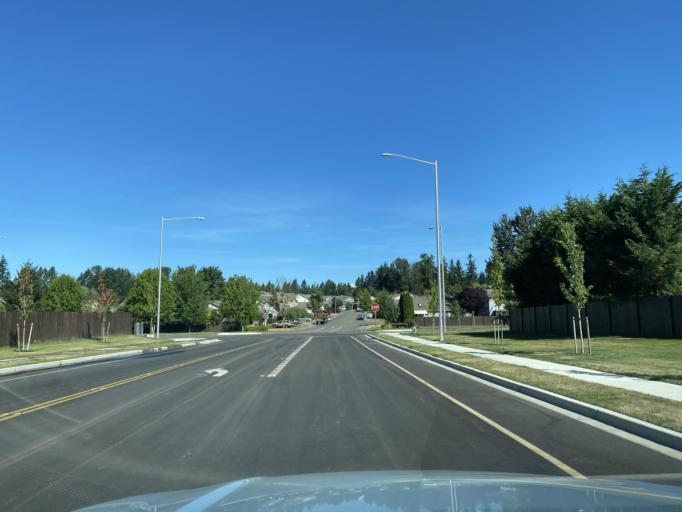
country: US
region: Washington
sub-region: Pierce County
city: South Hill
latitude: 47.0992
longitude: -122.2551
